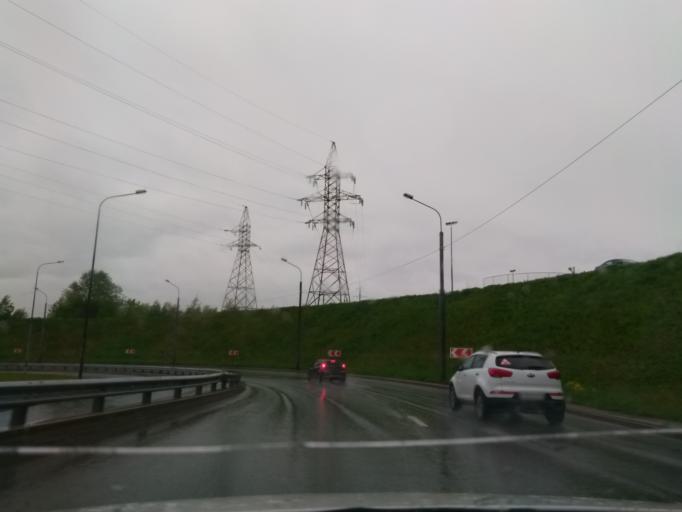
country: RU
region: Perm
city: Perm
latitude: 58.0087
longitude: 56.3219
